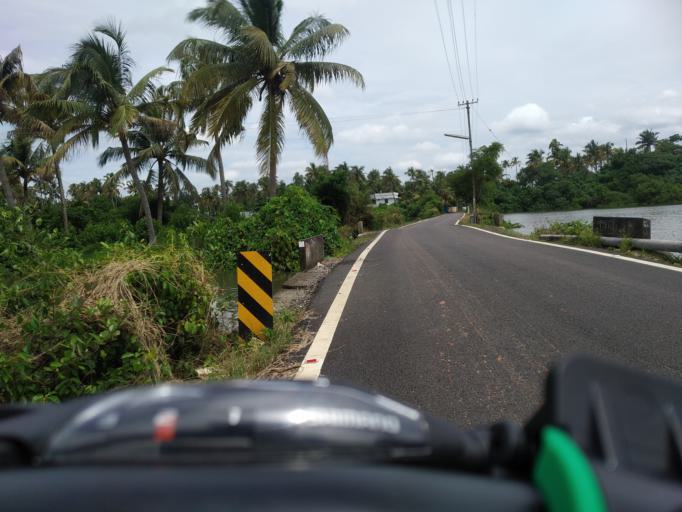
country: IN
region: Kerala
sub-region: Ernakulam
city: Elur
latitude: 10.0808
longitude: 76.2180
